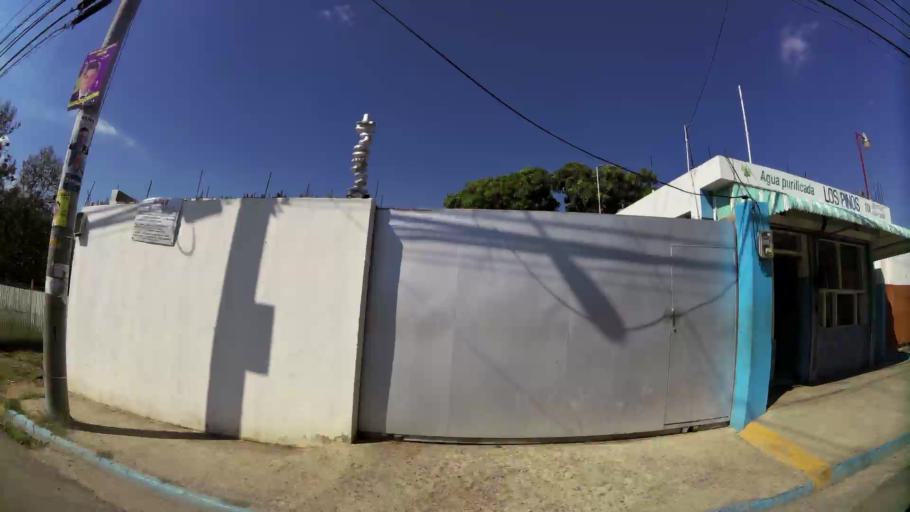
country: DO
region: Santo Domingo
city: Santo Domingo Oeste
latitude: 18.4725
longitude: -70.0055
